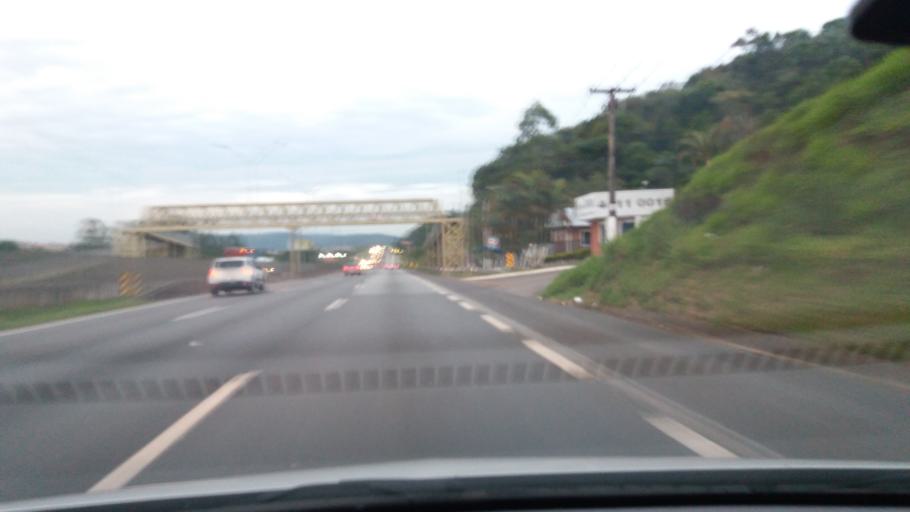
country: BR
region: Sao Paulo
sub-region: Atibaia
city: Atibaia
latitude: -23.1526
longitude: -46.5739
